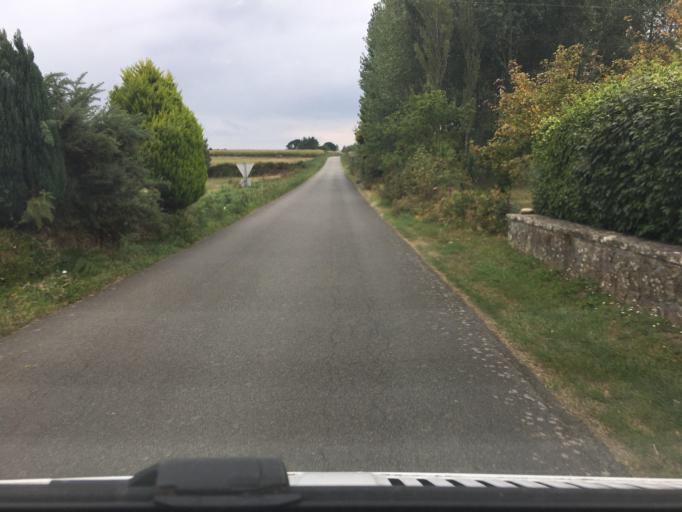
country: FR
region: Brittany
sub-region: Departement du Finistere
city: Beuzec-Cap-Sizun
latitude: 48.0742
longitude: -4.4753
